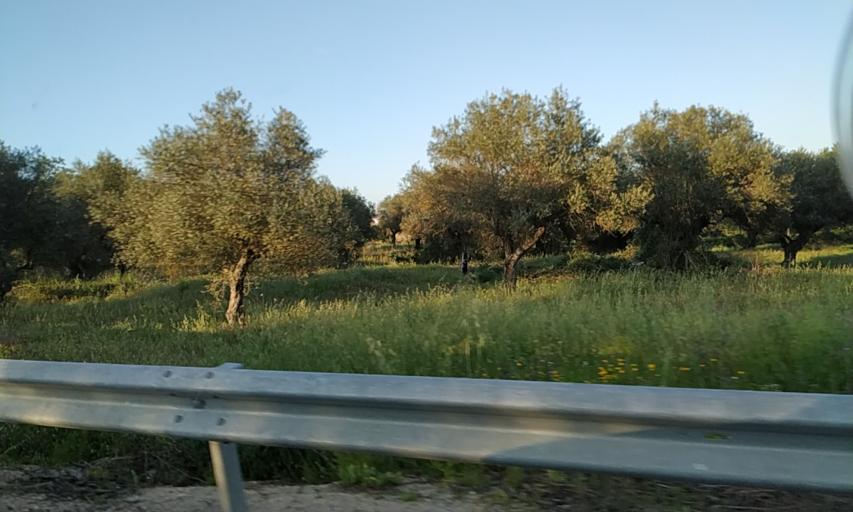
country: ES
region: Extremadura
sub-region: Provincia de Caceres
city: Valencia de Alcantara
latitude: 39.3995
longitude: -7.2507
